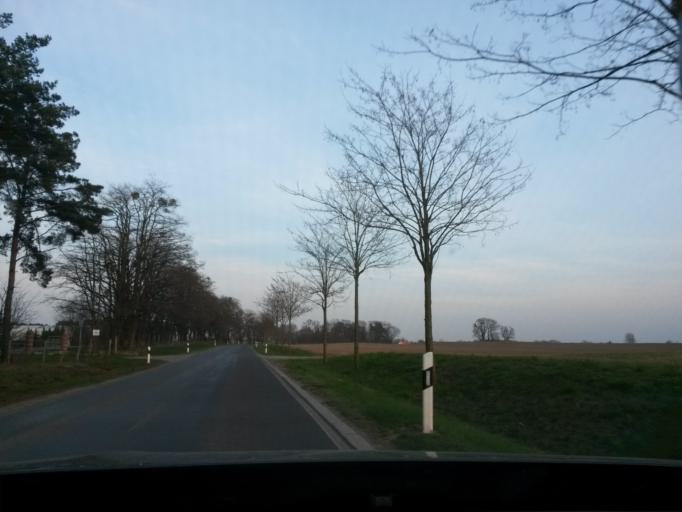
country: DE
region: Brandenburg
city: Strausberg
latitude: 52.5965
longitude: 13.9359
